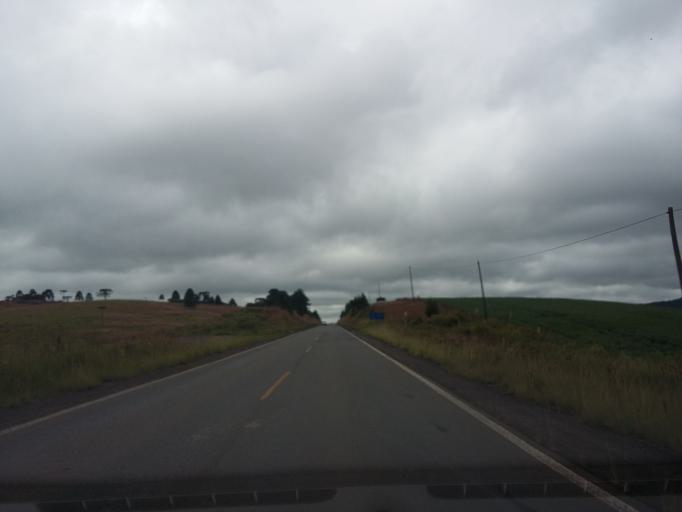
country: BR
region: Santa Catarina
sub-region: Lages
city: Lages
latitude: -27.8424
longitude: -50.2309
